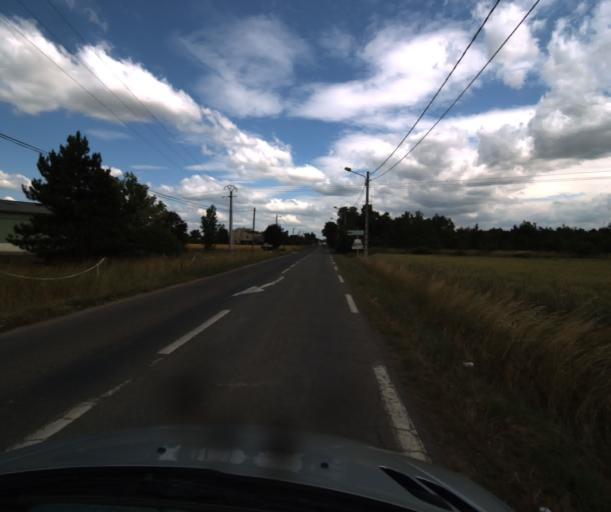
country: FR
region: Midi-Pyrenees
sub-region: Departement du Tarn-et-Garonne
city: Montauban
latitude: 43.9980
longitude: 1.3503
